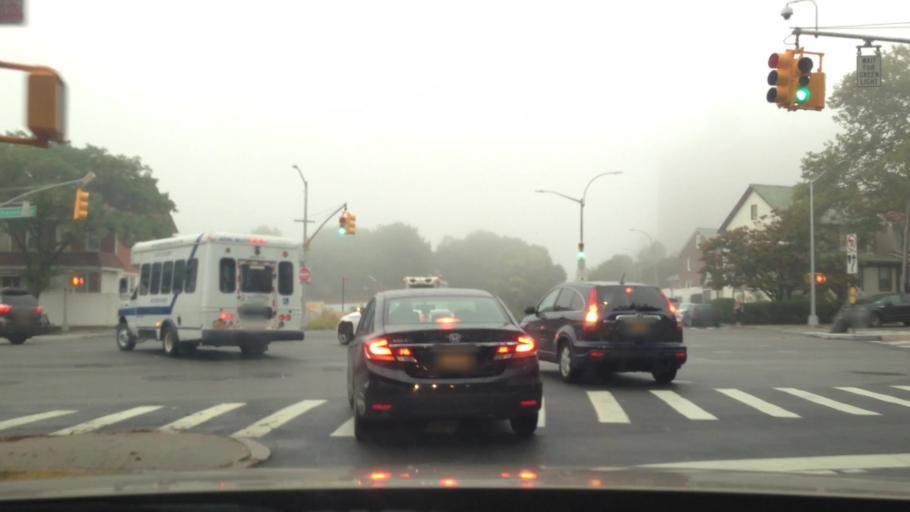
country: US
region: New York
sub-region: Queens County
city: Borough of Queens
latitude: 40.7054
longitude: -73.8586
